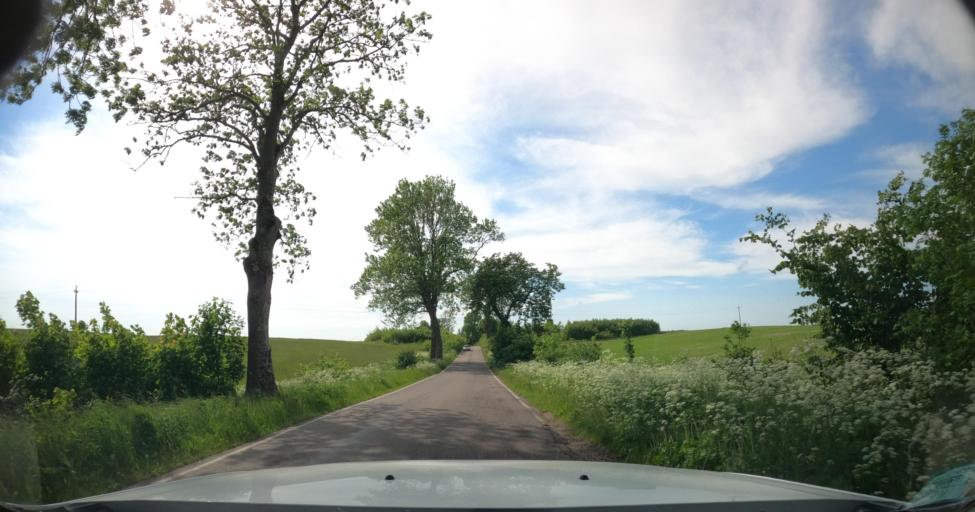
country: PL
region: Warmian-Masurian Voivodeship
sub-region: Powiat ostrodzki
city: Milakowo
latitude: 54.0087
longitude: 20.1351
